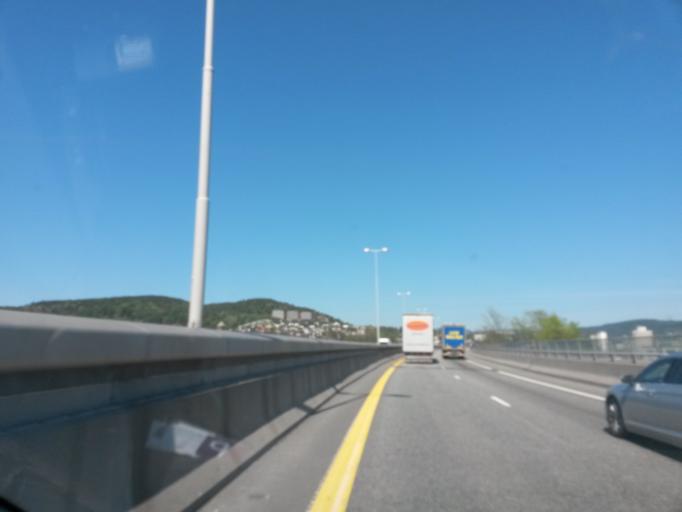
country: NO
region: Buskerud
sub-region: Drammen
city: Drammen
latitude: 59.7324
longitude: 10.2156
